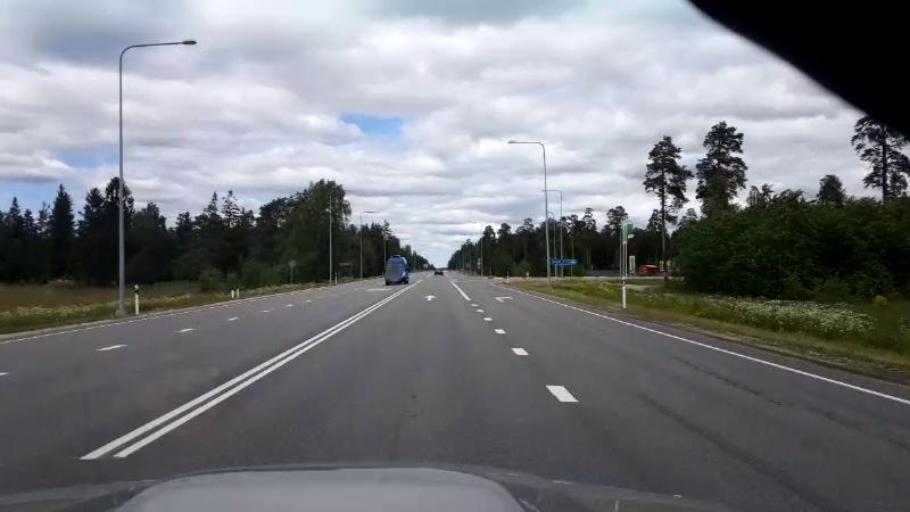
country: EE
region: Raplamaa
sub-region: Maerjamaa vald
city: Marjamaa
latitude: 58.9289
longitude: 24.4616
